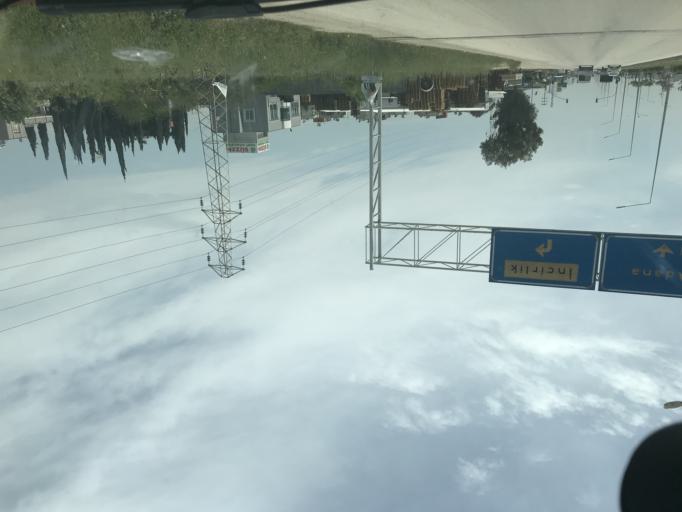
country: TR
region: Adana
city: Yuregir
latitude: 36.9822
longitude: 35.4325
